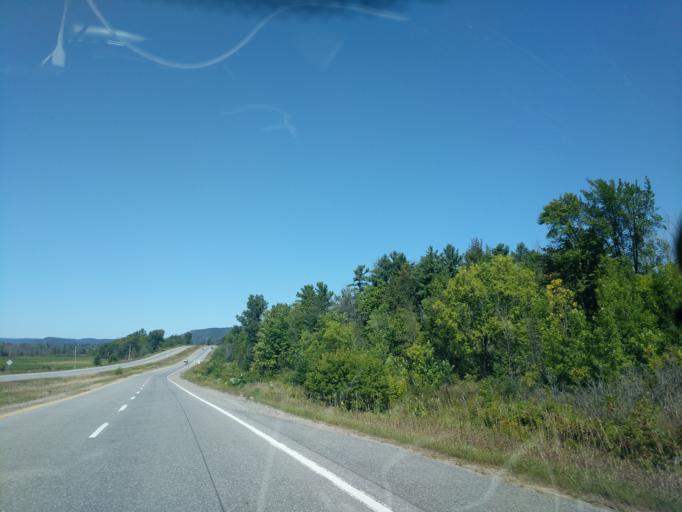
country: CA
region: Quebec
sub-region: Outaouais
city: Wakefield
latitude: 45.5091
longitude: -75.9747
